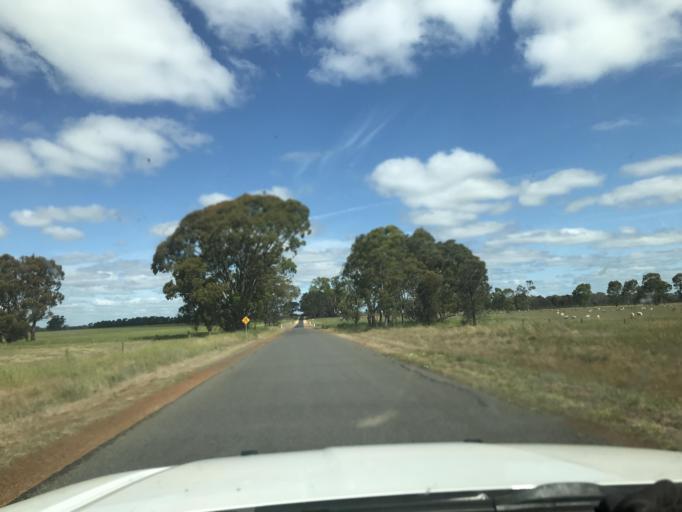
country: AU
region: South Australia
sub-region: Naracoorte and Lucindale
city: Naracoorte
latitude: -36.9932
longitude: 141.2917
